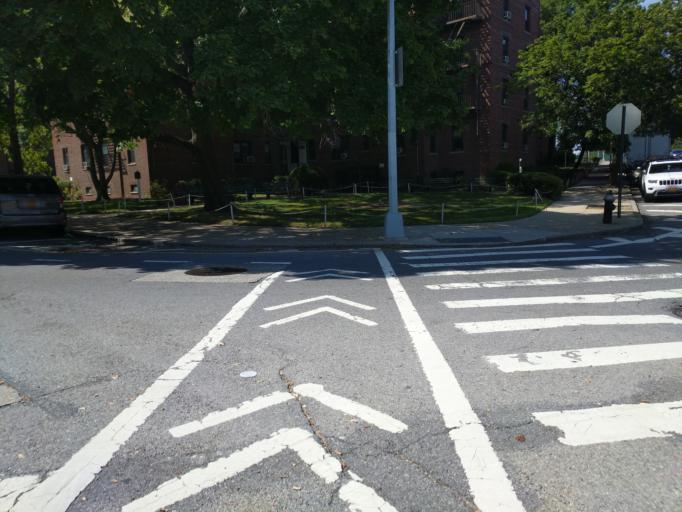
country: US
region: New York
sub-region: Queens County
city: Borough of Queens
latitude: 40.7572
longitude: -73.8552
